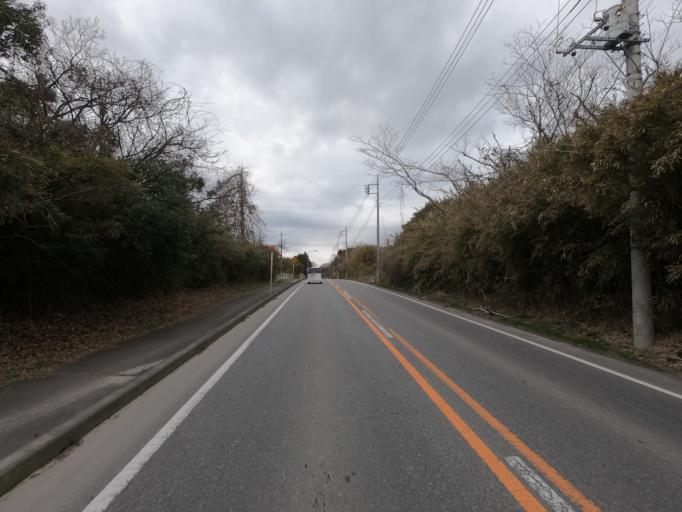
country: JP
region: Ibaraki
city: Ishioka
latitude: 36.0957
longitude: 140.3648
